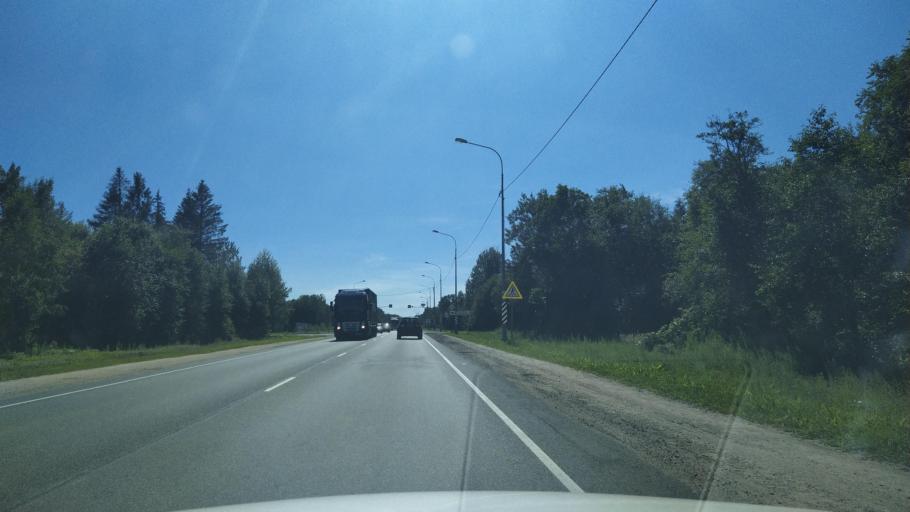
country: RU
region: Pskov
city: Pskov
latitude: 57.7875
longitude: 28.4100
